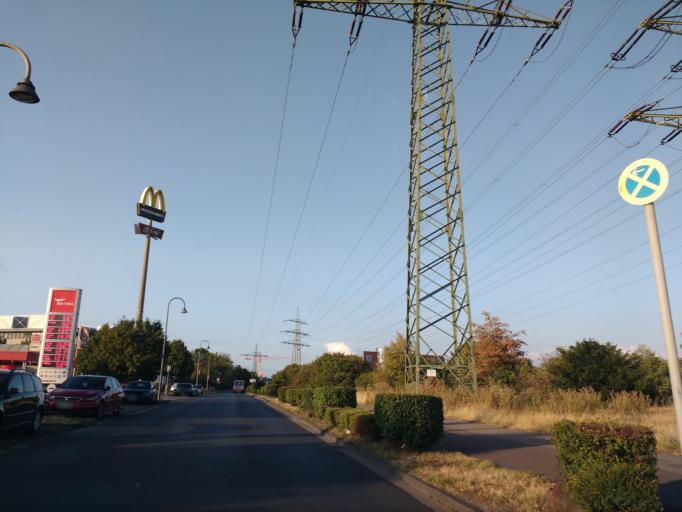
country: DE
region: North Rhine-Westphalia
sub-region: Regierungsbezirk Koln
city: Gremberghoven
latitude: 50.9108
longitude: 7.0531
